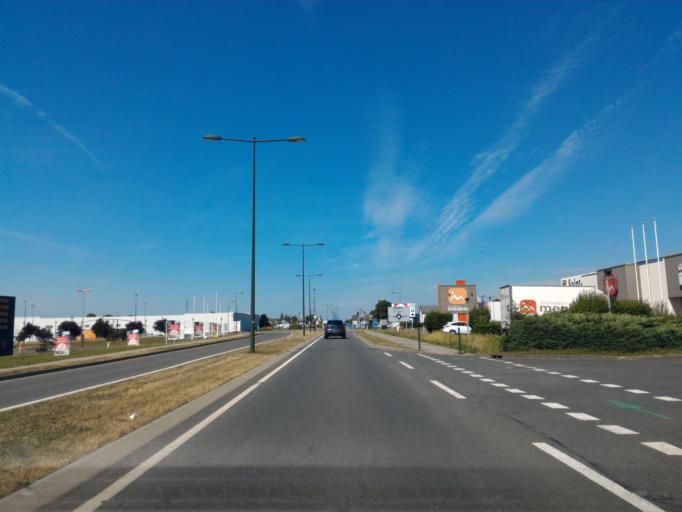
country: FR
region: Centre
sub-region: Departement de l'Indre
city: Saint-Maur
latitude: 46.7808
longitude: 1.6532
